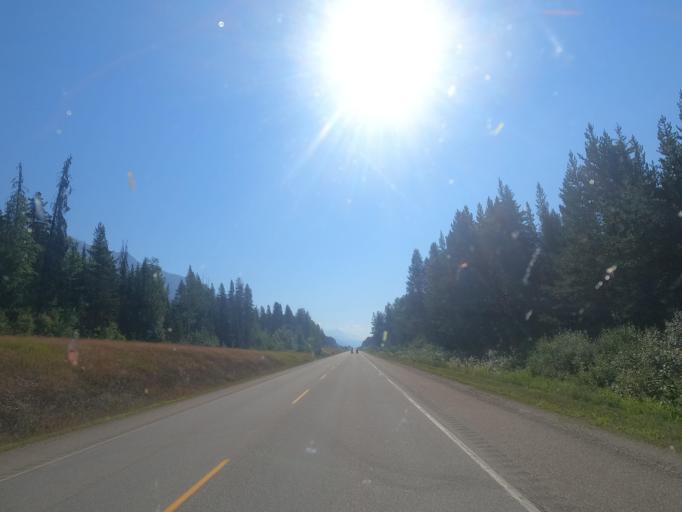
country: CA
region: Alberta
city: Grande Cache
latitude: 52.9890
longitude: -119.0054
